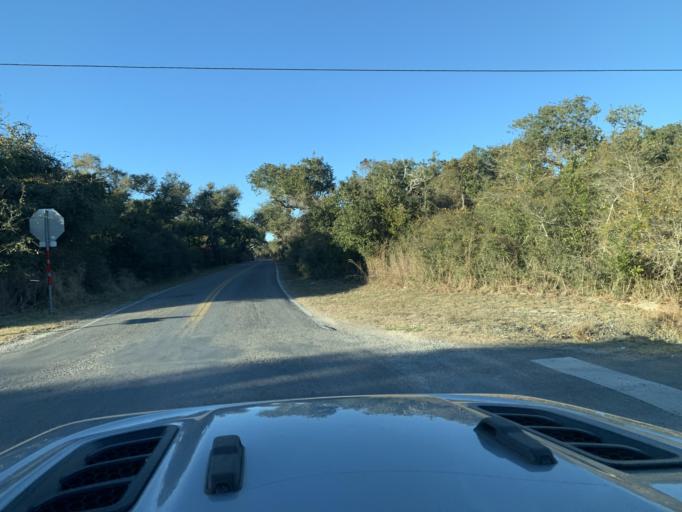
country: US
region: Texas
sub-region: Aransas County
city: Fulton
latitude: 28.1474
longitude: -96.9842
